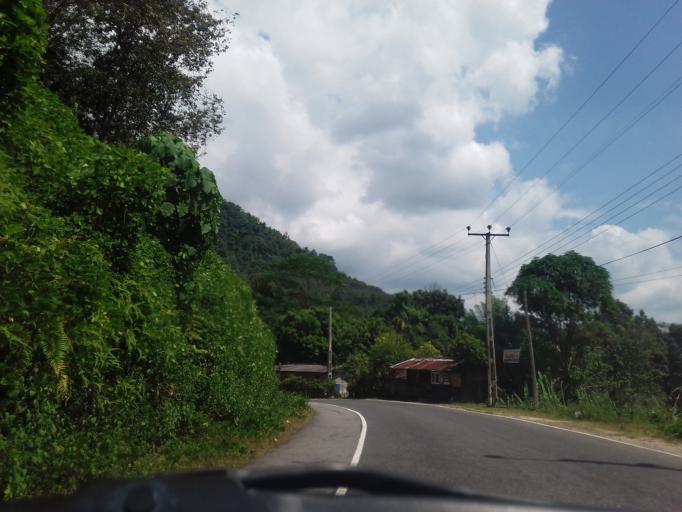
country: LK
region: Central
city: Hatton
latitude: 6.9964
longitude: 80.3522
